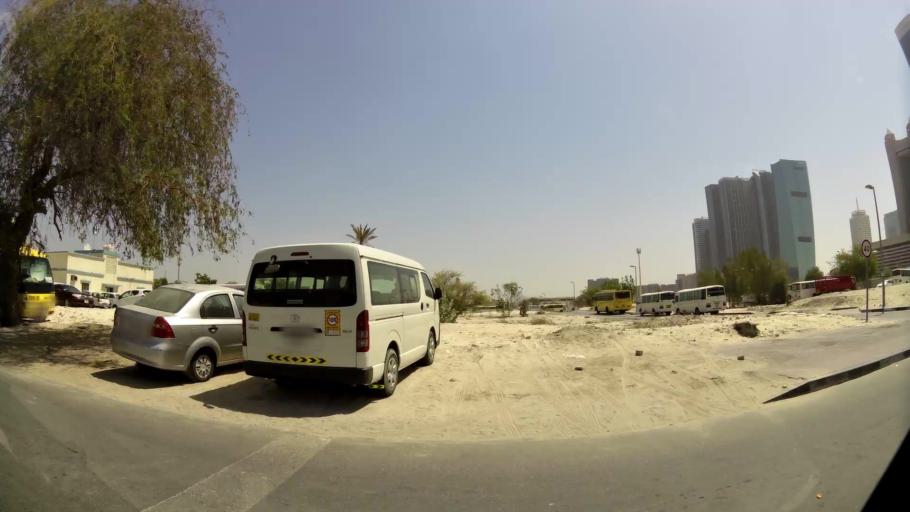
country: AE
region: Ash Shariqah
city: Sharjah
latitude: 25.2271
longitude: 55.2789
